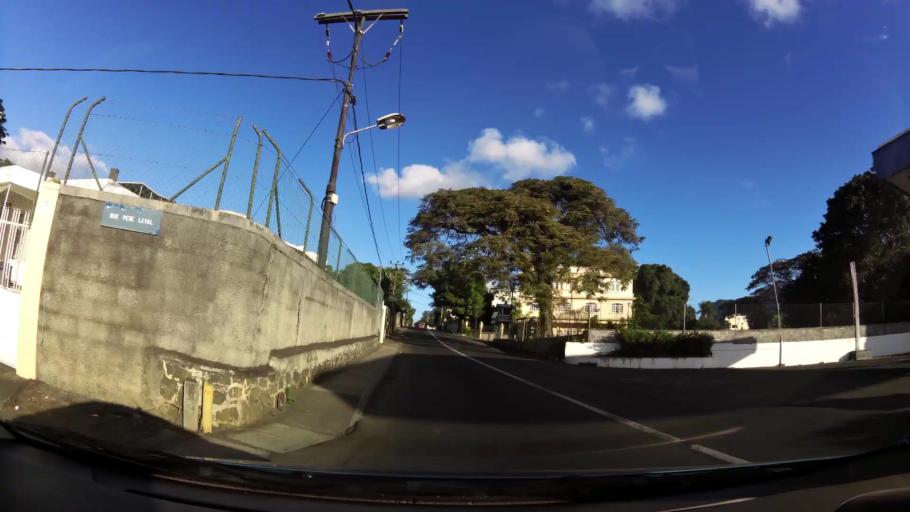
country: MU
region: Plaines Wilhems
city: Ebene
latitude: -20.2365
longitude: 57.4629
